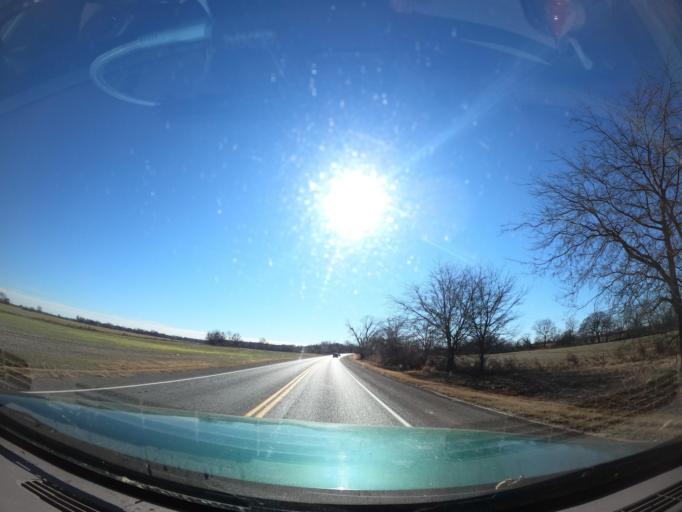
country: US
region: Oklahoma
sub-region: Muskogee County
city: Haskell
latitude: 35.8816
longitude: -95.6601
